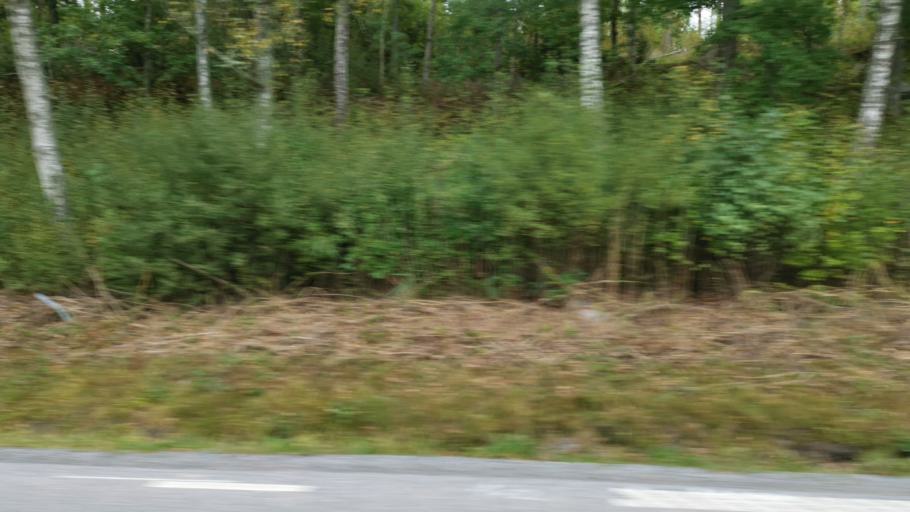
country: SE
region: Vaestra Goetaland
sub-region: Tanums Kommun
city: Tanumshede
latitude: 58.7021
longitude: 11.3382
